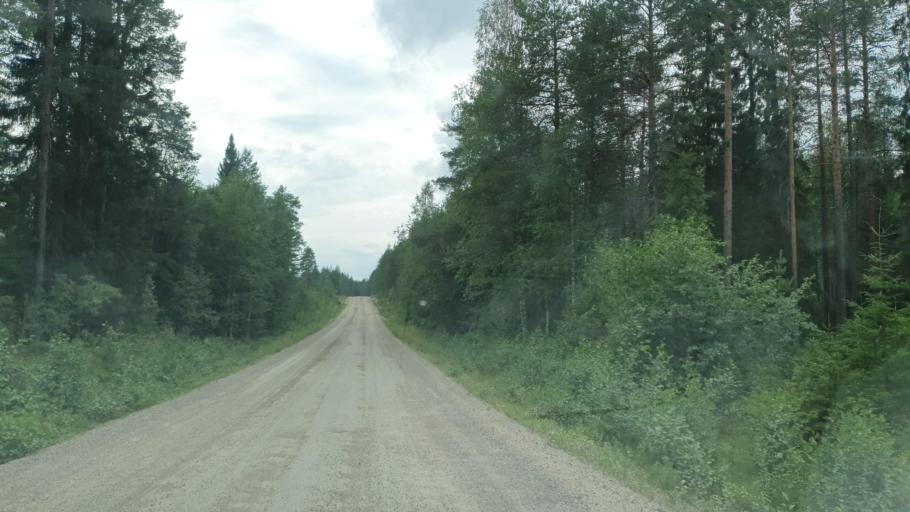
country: FI
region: Kainuu
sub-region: Kehys-Kainuu
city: Kuhmo
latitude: 64.7308
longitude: 29.7215
